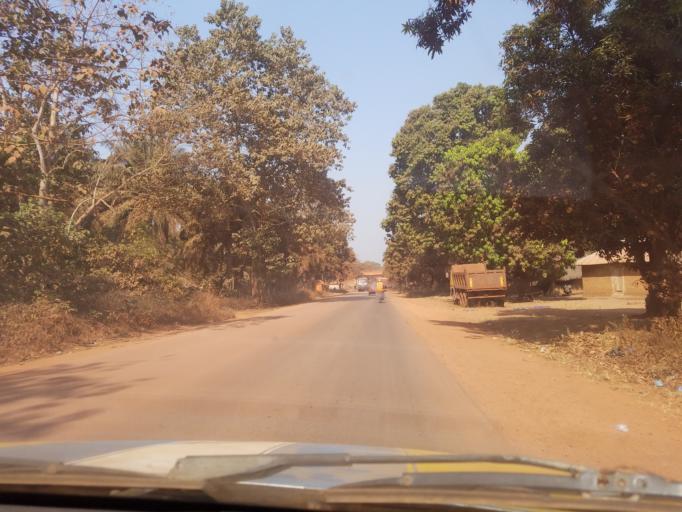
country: GN
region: Boke
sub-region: Boke Prefecture
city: Sangueya
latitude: 10.8095
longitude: -14.3857
